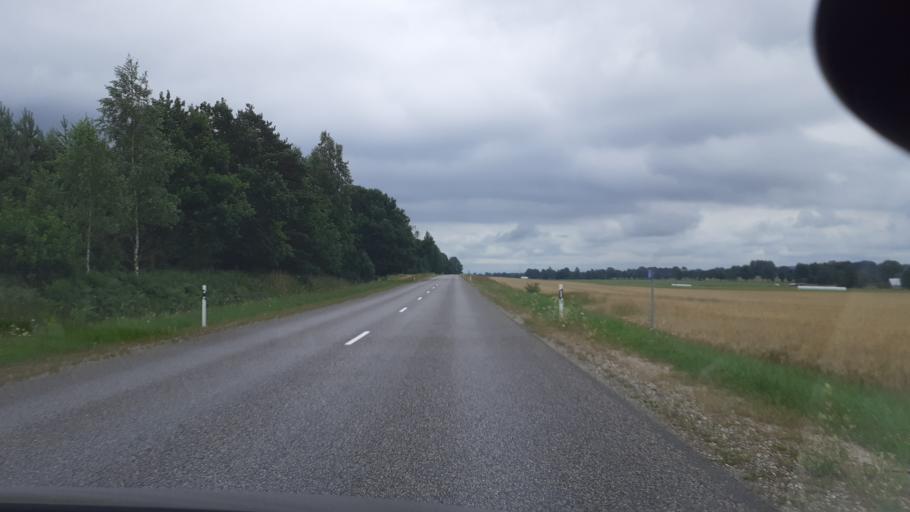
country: LV
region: Kuldigas Rajons
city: Kuldiga
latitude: 57.0294
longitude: 21.8505
